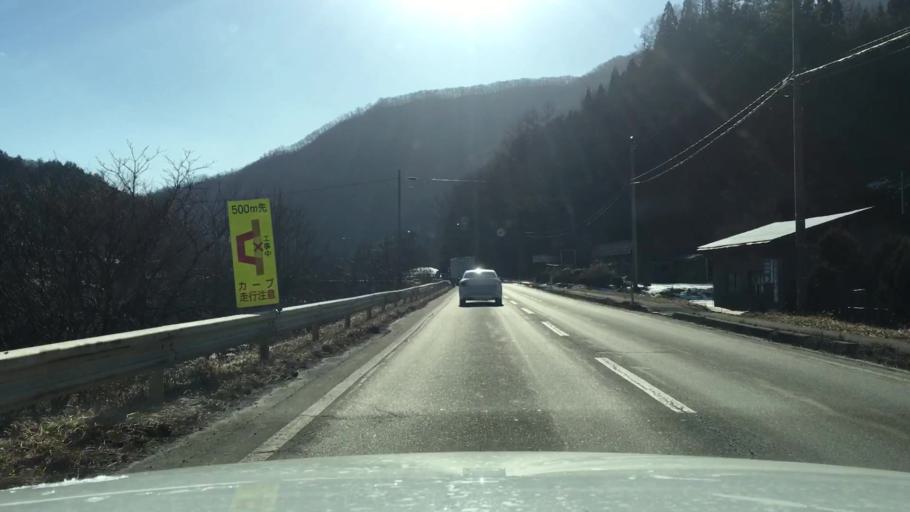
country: JP
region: Iwate
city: Tono
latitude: 39.6168
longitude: 141.6245
